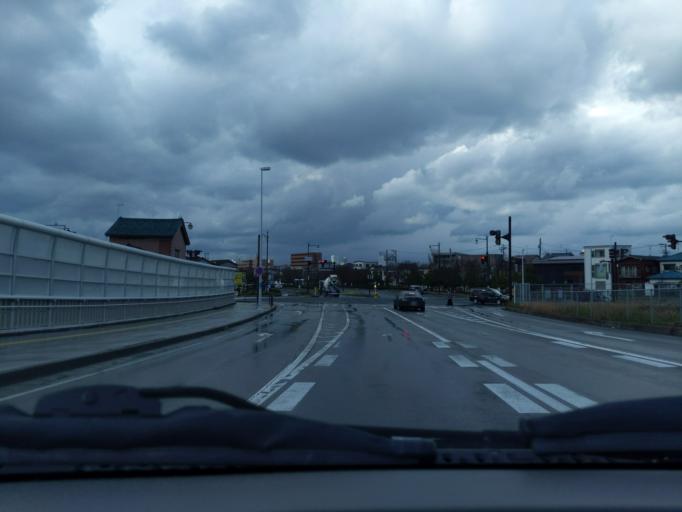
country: JP
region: Niigata
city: Niigata-shi
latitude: 37.9247
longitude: 139.0532
